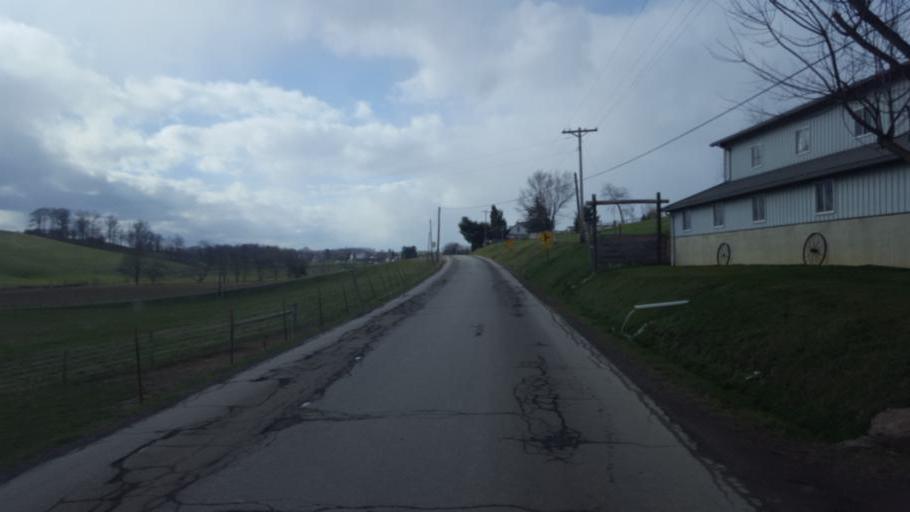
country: US
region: Ohio
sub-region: Tuscarawas County
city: Sugarcreek
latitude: 40.4963
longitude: -81.6981
